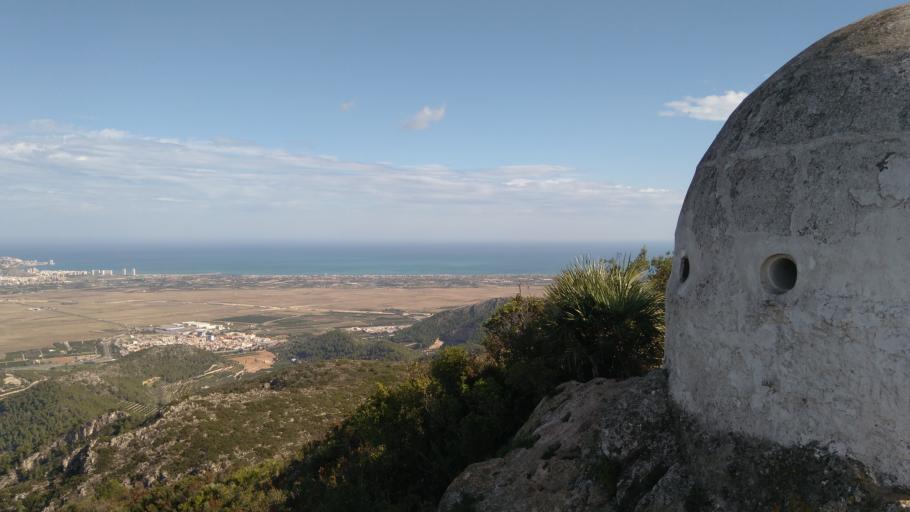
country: ES
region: Valencia
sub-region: Provincia de Valencia
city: Llauri
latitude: 39.1118
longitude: -0.3246
